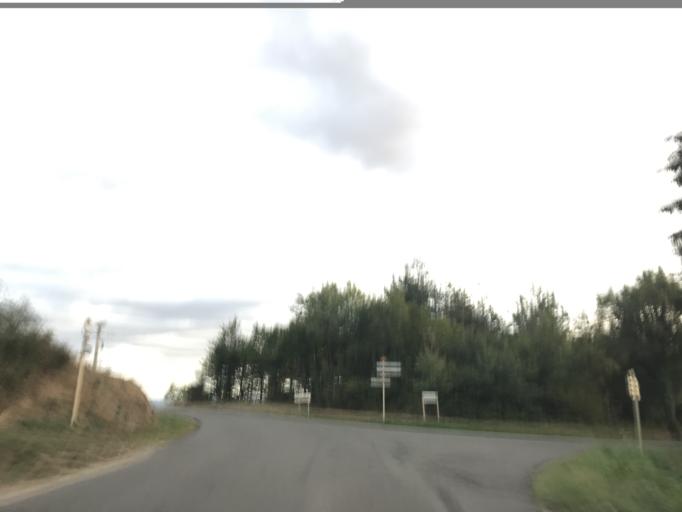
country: FR
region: Auvergne
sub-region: Departement du Puy-de-Dome
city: Escoutoux
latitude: 45.8252
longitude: 3.5576
